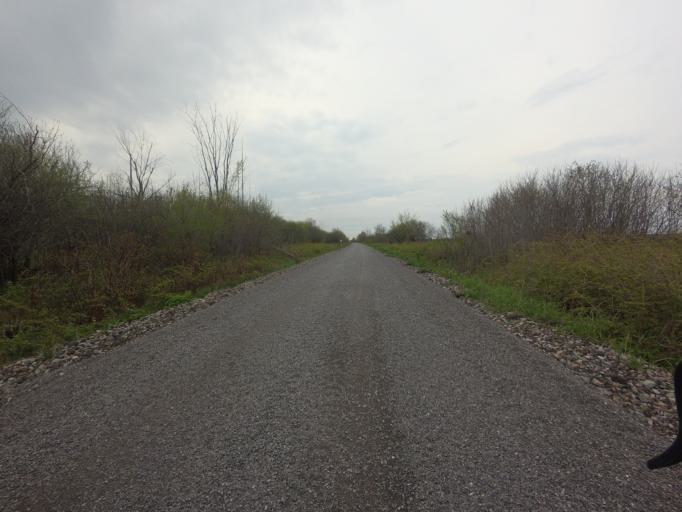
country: CA
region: Ontario
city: Carleton Place
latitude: 45.2056
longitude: -76.1713
